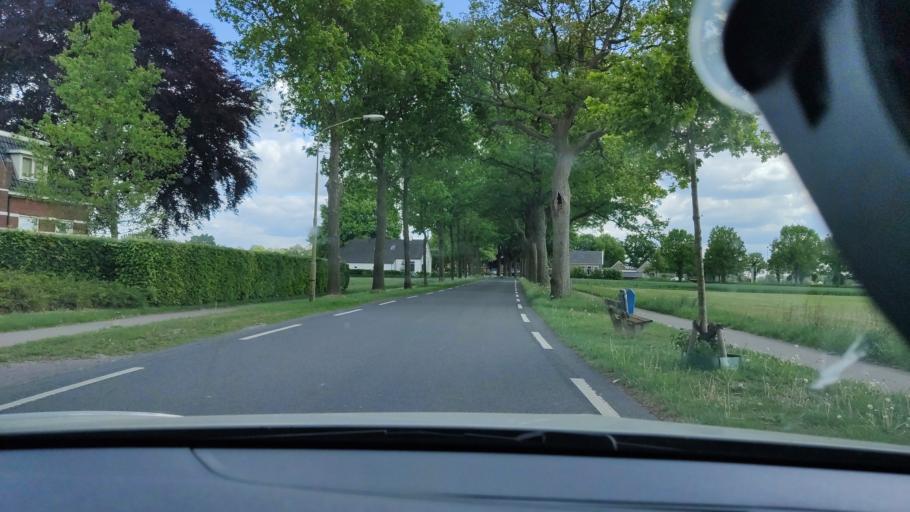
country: NL
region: Drenthe
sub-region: Gemeente Tynaarlo
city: Zuidlaren
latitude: 53.1236
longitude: 6.6603
